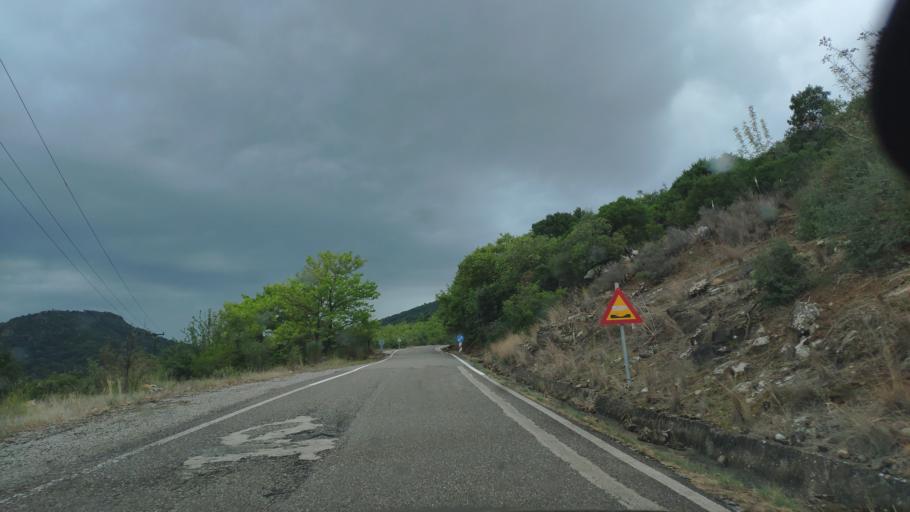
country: GR
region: West Greece
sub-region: Nomos Aitolias kai Akarnanias
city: Lepenou
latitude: 38.8118
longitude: 21.3343
